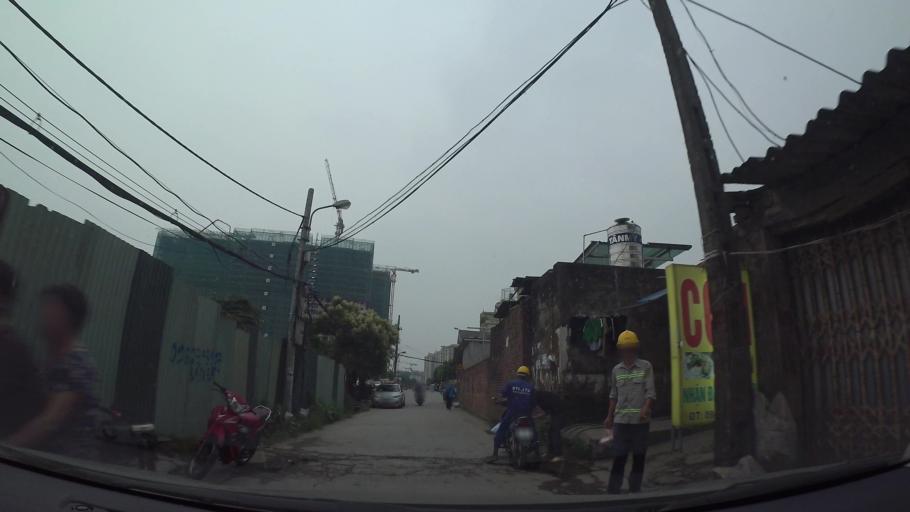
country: VN
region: Ha Noi
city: Trau Quy
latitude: 21.0428
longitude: 105.9020
